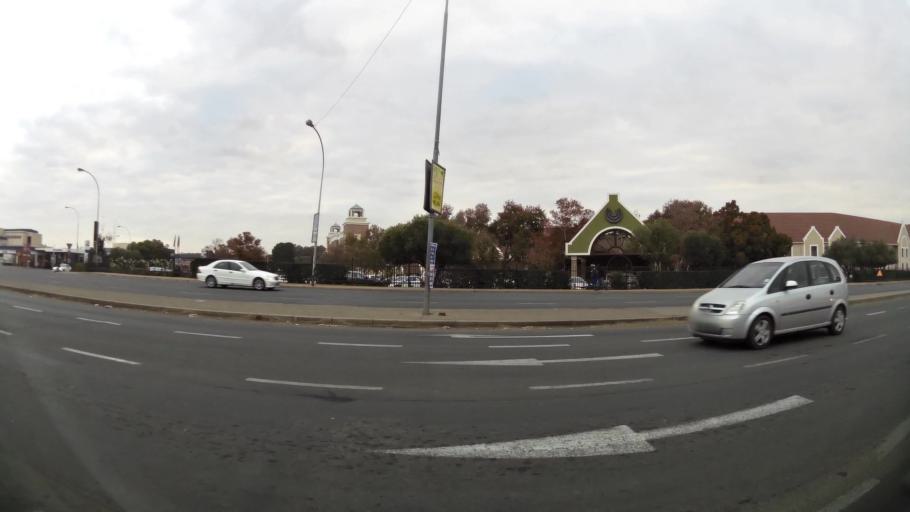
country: ZA
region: Orange Free State
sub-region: Mangaung Metropolitan Municipality
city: Bloemfontein
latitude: -29.1091
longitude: 26.1991
